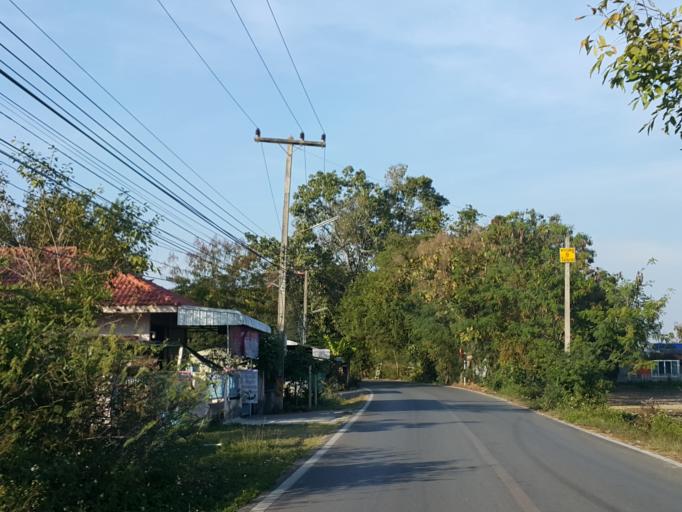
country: TH
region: Chiang Mai
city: San Sai
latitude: 18.7910
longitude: 99.0608
